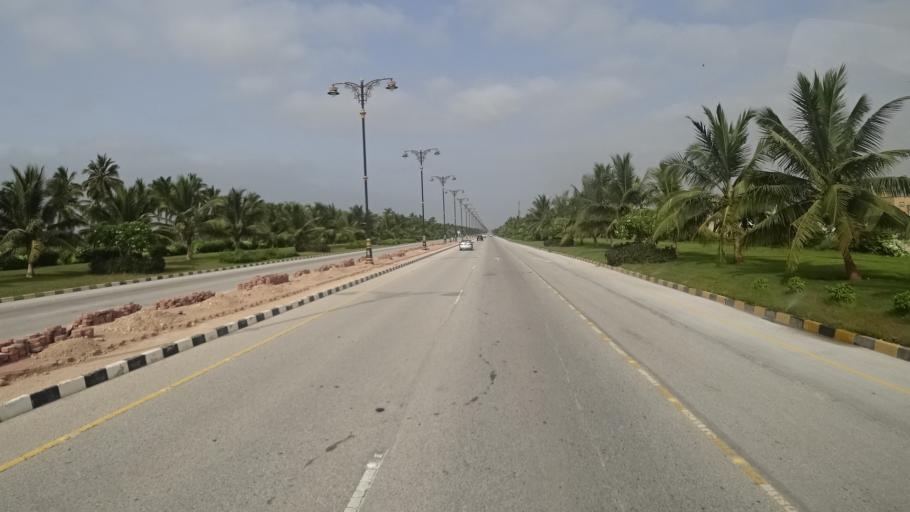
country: OM
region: Zufar
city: Salalah
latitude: 17.0471
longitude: 54.2110
